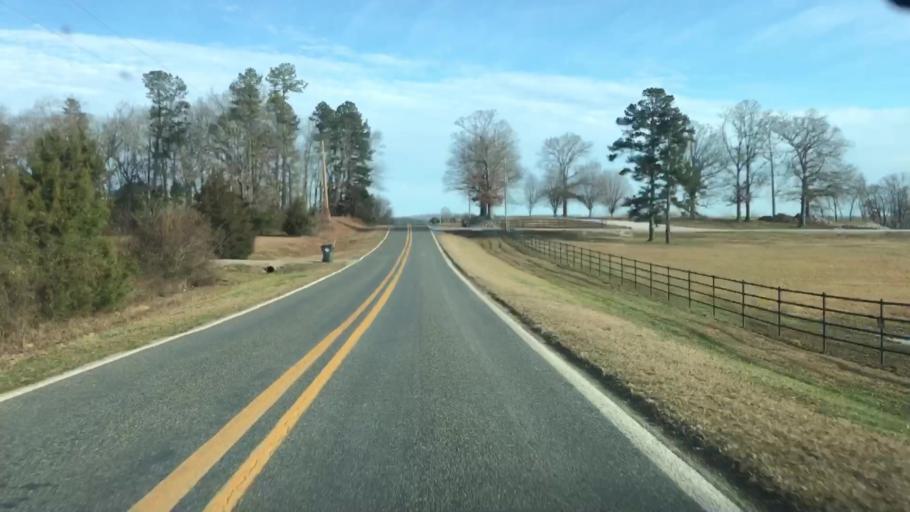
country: US
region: Arkansas
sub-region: Garland County
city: Rockwell
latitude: 34.5015
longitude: -93.2763
